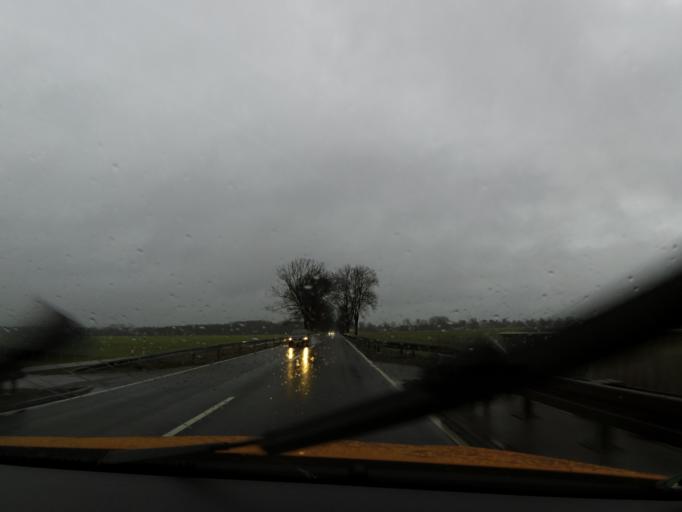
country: DE
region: Brandenburg
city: Rangsdorf
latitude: 52.2628
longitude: 13.4563
